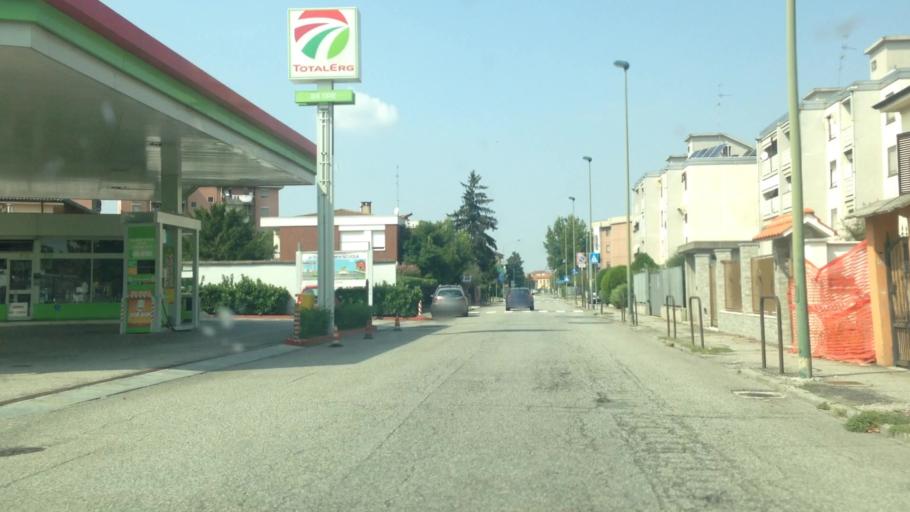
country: IT
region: Piedmont
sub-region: Provincia di Alessandria
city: Casale Monferrato
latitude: 45.1312
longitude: 8.4723
